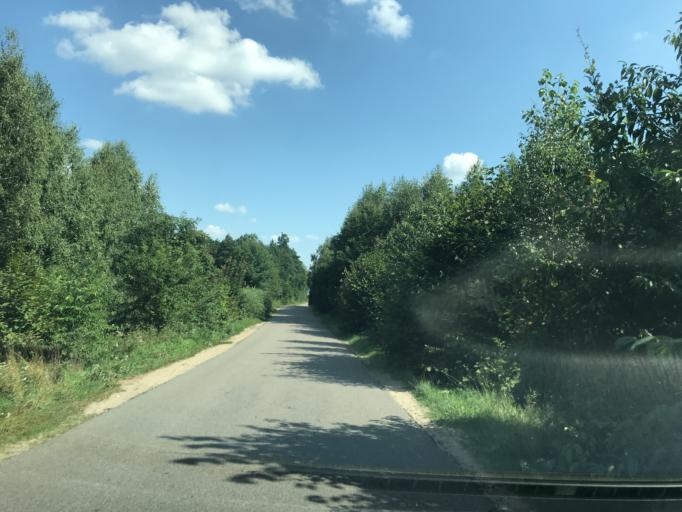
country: PL
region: Masovian Voivodeship
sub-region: Powiat zurominski
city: Lubowidz
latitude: 53.1583
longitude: 19.9106
